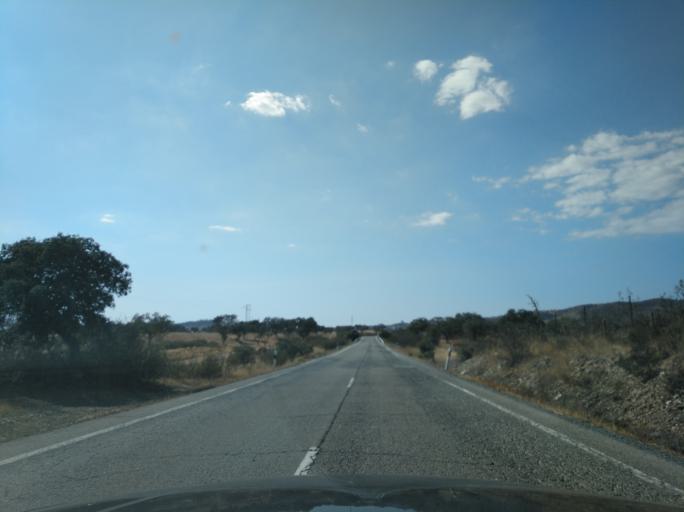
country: ES
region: Andalusia
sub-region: Provincia de Huelva
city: Santa Barbara de Casa
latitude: 37.7759
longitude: -7.1503
